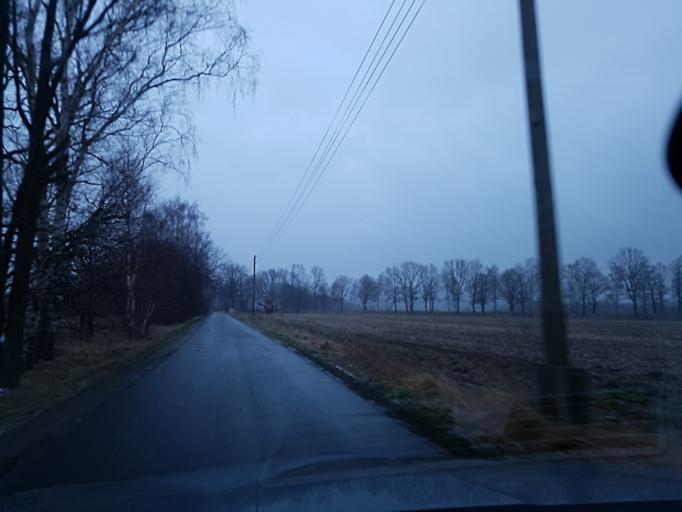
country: DE
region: Brandenburg
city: Groden
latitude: 51.4299
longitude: 13.5586
